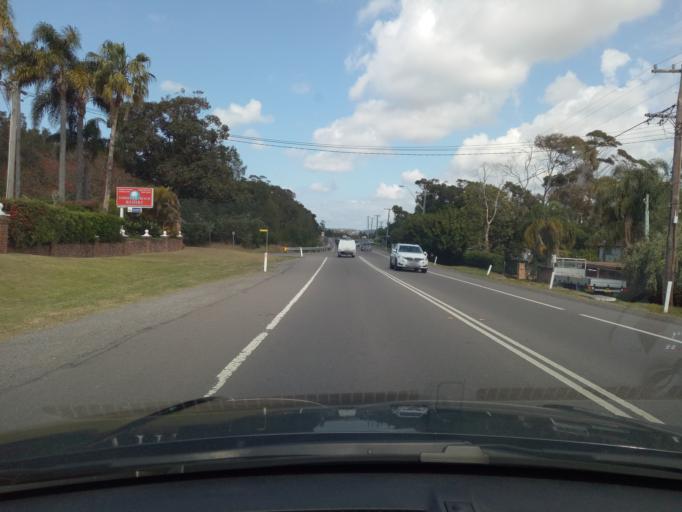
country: AU
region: New South Wales
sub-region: Gosford Shire
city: Forresters Beach
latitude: -33.4065
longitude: 151.4644
